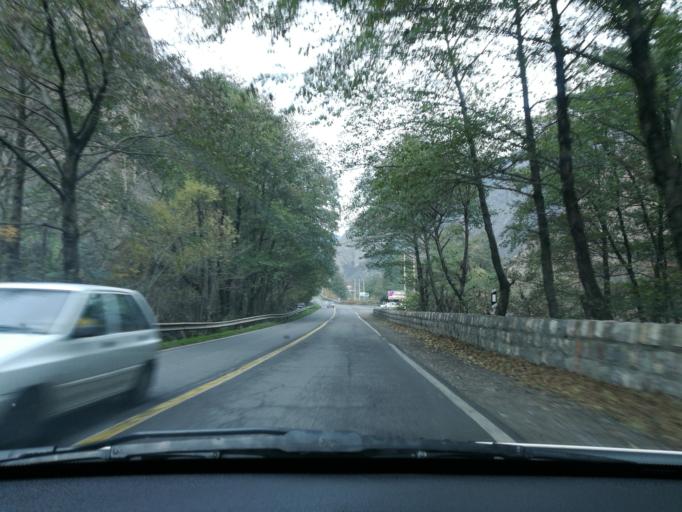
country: IR
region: Mazandaran
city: Chalus
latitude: 36.3522
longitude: 51.2609
